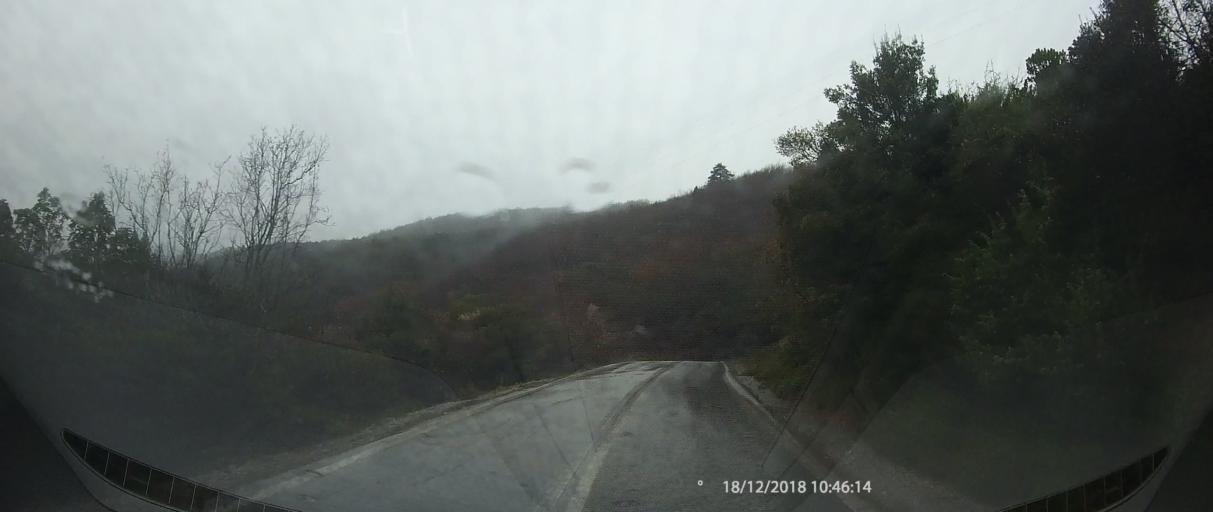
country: GR
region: Central Macedonia
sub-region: Nomos Pierias
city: Kato Milia
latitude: 40.1886
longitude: 22.3249
